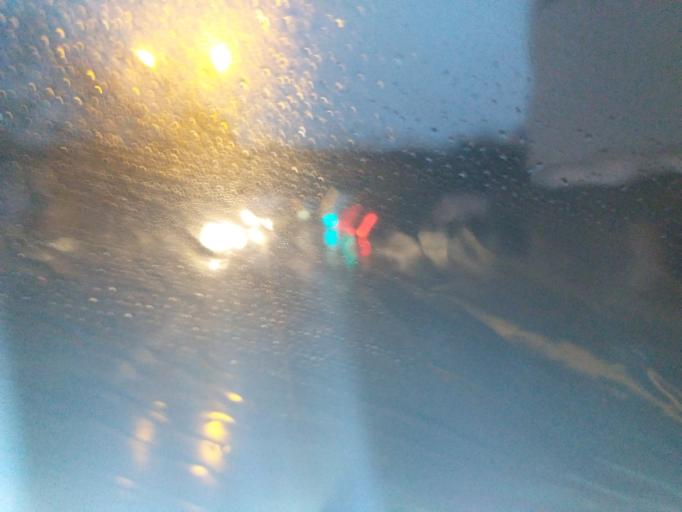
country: TR
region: Ankara
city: Ankara
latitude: 39.9436
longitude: 32.8280
